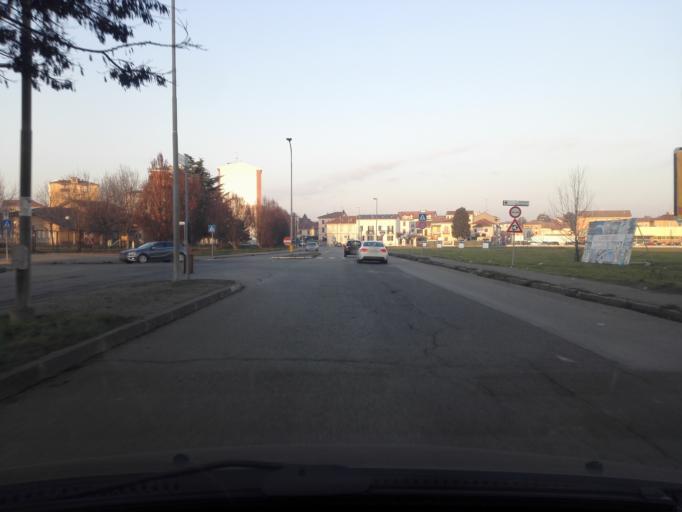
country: IT
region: Piedmont
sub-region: Provincia di Alessandria
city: Alessandria
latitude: 44.8995
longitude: 8.6066
